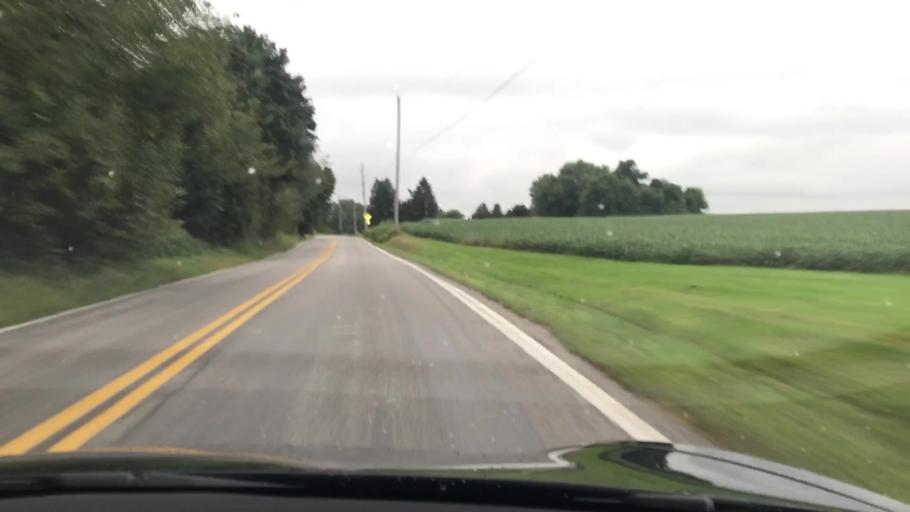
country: US
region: Pennsylvania
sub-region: York County
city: Dover
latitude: 39.9590
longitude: -76.8685
